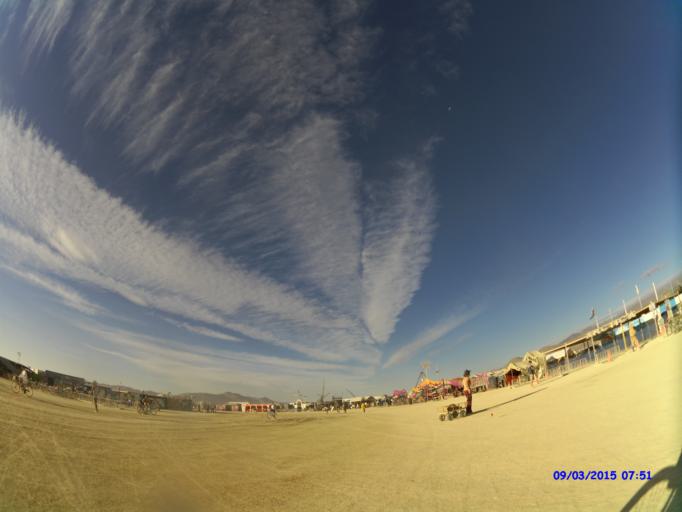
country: US
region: Nevada
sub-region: Pershing County
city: Lovelock
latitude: 40.7814
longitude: -119.2147
